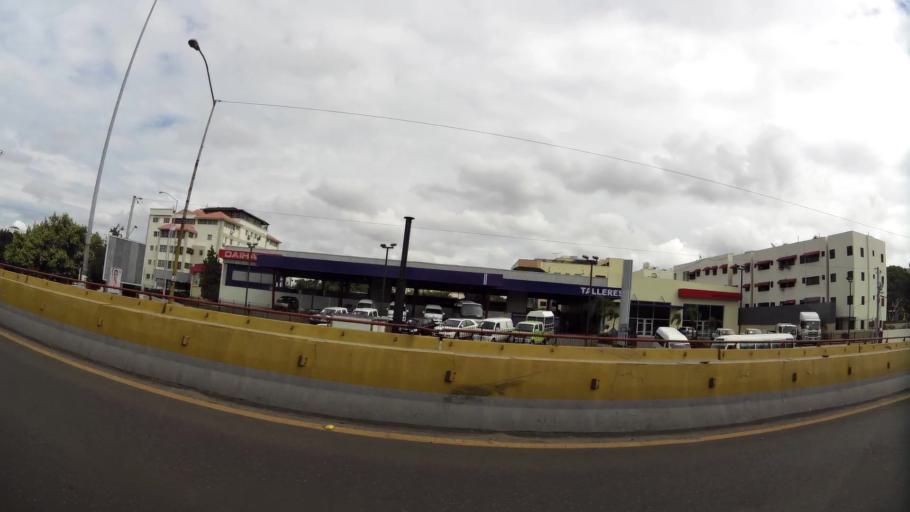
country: DO
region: Santiago
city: Santiago de los Caballeros
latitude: 19.4492
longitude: -70.6834
